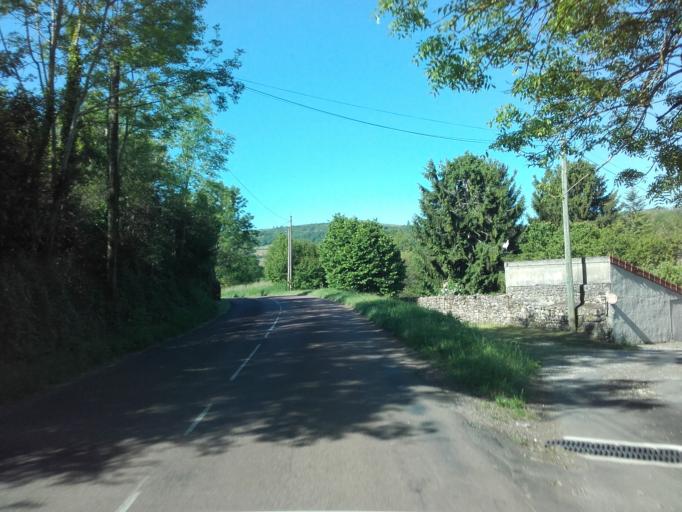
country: FR
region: Bourgogne
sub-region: Departement de la Cote-d'Or
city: Nolay
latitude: 46.9457
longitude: 4.6305
